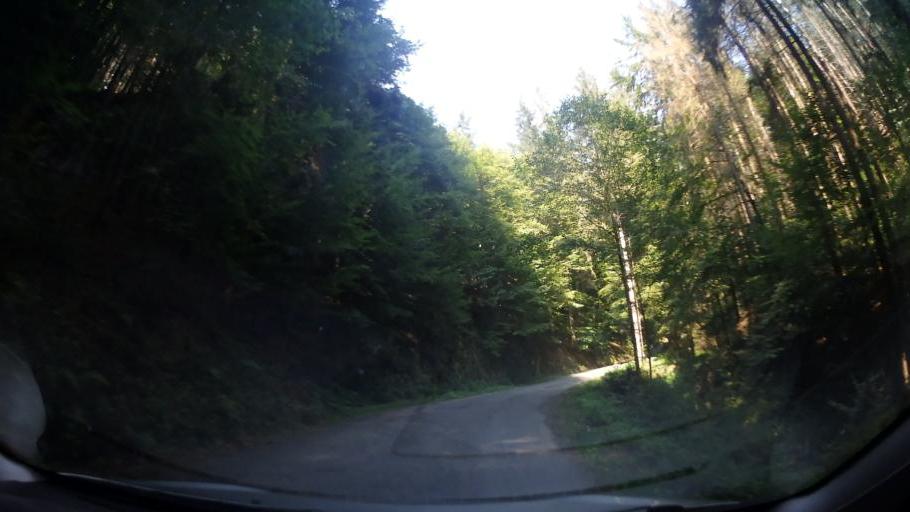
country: CZ
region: South Moravian
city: Olesnice
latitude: 49.5363
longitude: 16.3529
